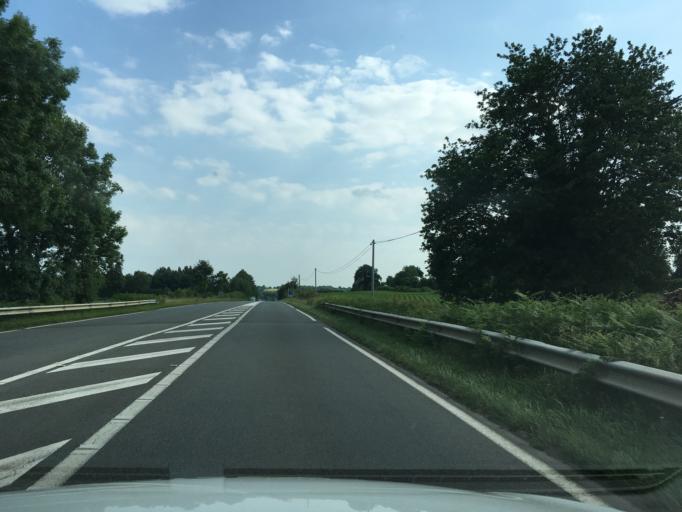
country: FR
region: Poitou-Charentes
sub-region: Departement des Deux-Sevres
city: Saint-Pardoux
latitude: 46.5978
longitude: -0.2891
